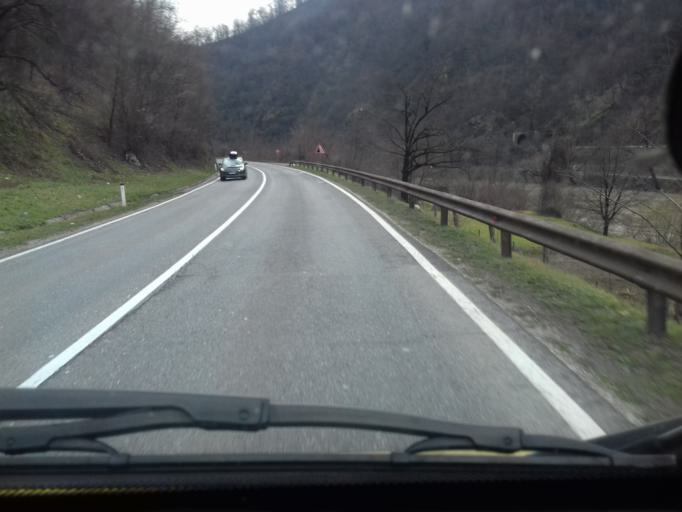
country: BA
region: Federation of Bosnia and Herzegovina
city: Zeljezno Polje
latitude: 44.3106
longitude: 17.9031
